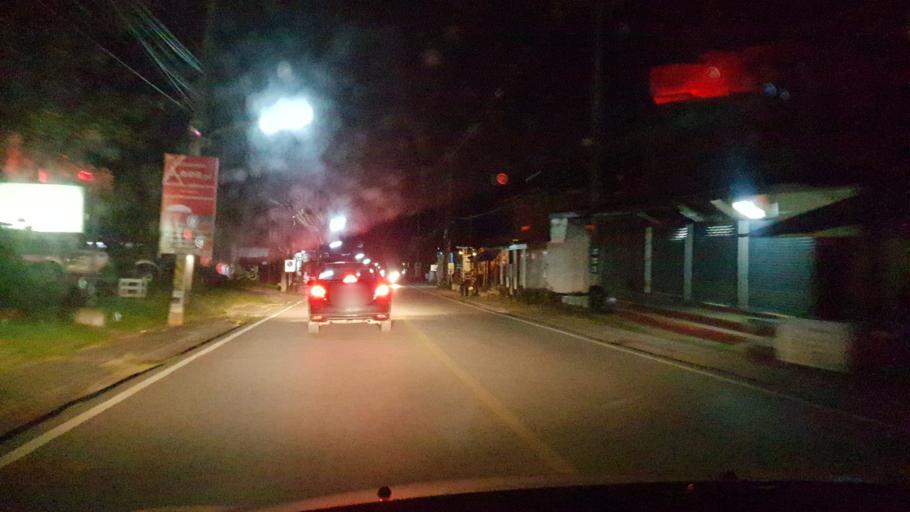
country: TH
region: Mae Hong Son
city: Khun Yuam
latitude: 18.8244
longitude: 97.9344
